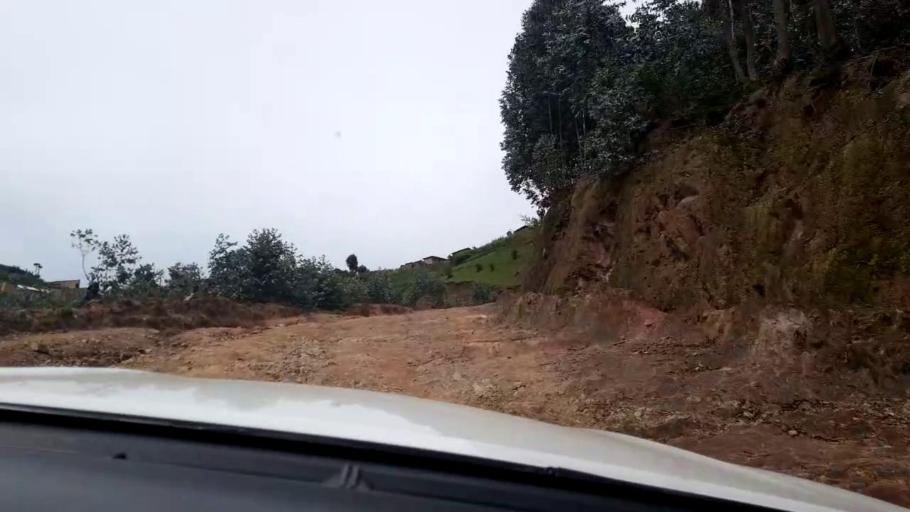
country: RW
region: Western Province
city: Kibuye
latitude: -1.8868
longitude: 29.4539
